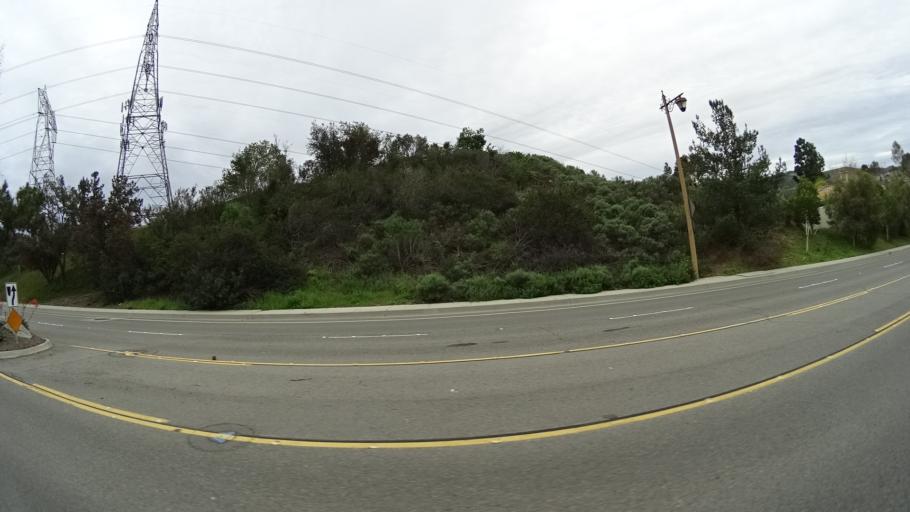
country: US
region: California
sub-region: Orange County
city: Villa Park
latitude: 33.8481
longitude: -117.7603
